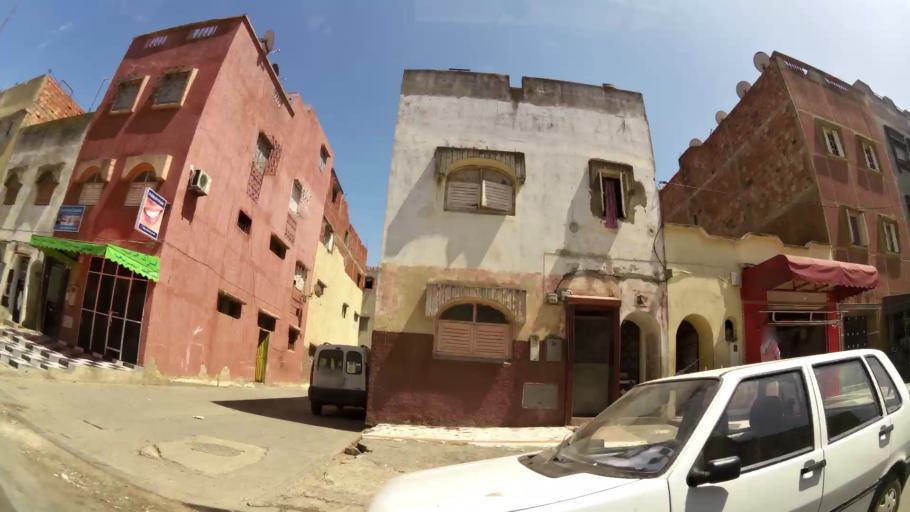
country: MA
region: Gharb-Chrarda-Beni Hssen
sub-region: Kenitra Province
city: Kenitra
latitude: 34.2462
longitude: -6.5466
